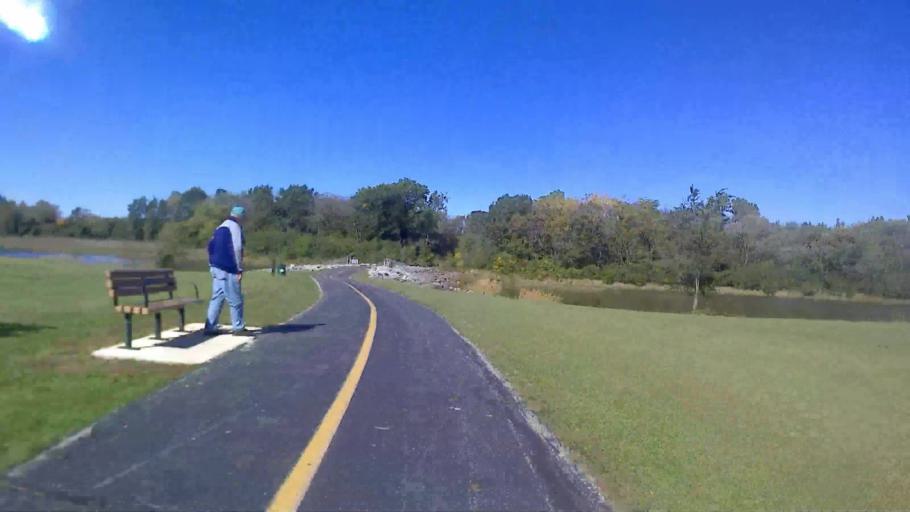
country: US
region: Illinois
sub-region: Cook County
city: Rolling Meadows
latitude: 42.0309
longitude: -88.0198
